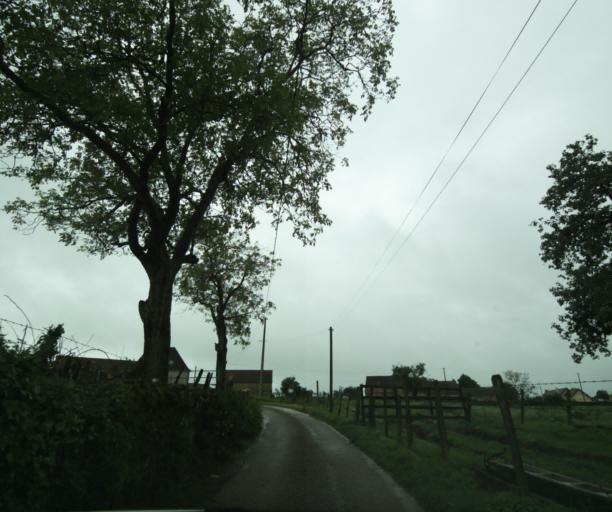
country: FR
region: Bourgogne
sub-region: Departement de Saone-et-Loire
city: Charolles
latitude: 46.3819
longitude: 4.2211
